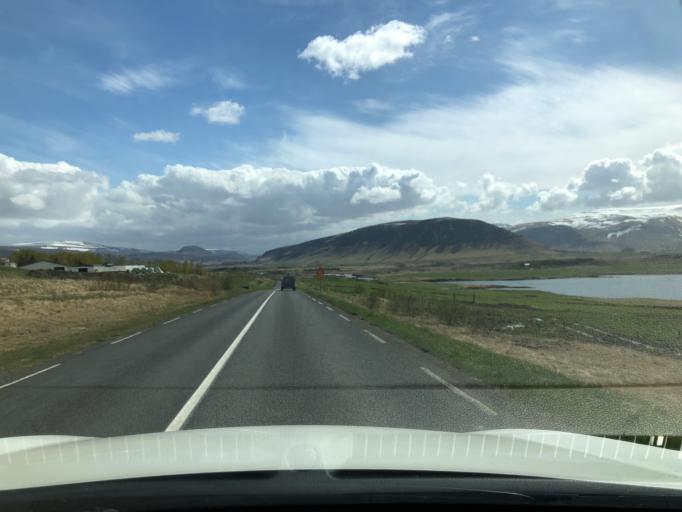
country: IS
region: Capital Region
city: Mosfellsbaer
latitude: 64.3506
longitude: -21.6318
